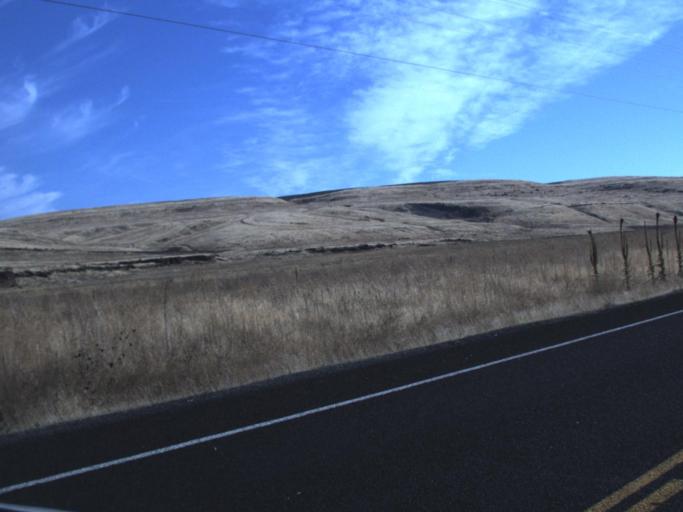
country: US
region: Washington
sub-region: Franklin County
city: Connell
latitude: 46.6498
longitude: -118.5989
